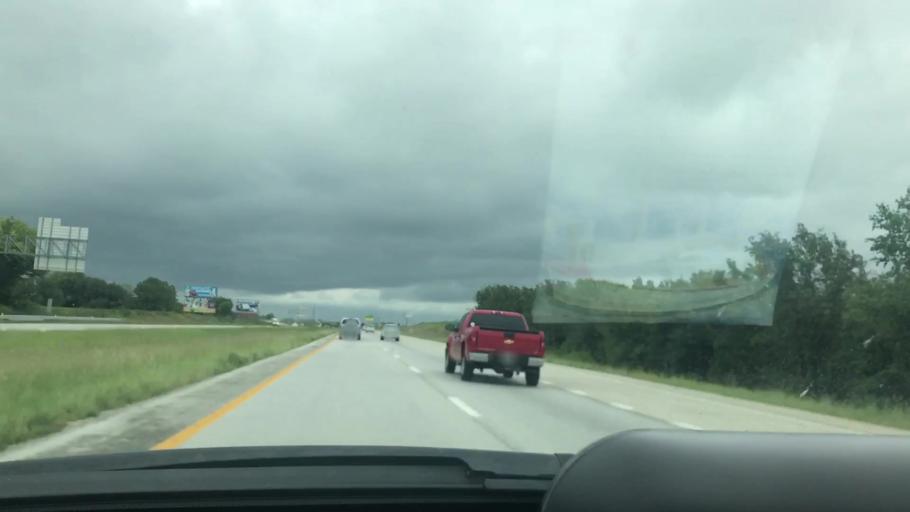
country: US
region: Missouri
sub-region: Jasper County
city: Duenweg
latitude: 37.0660
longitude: -94.4123
